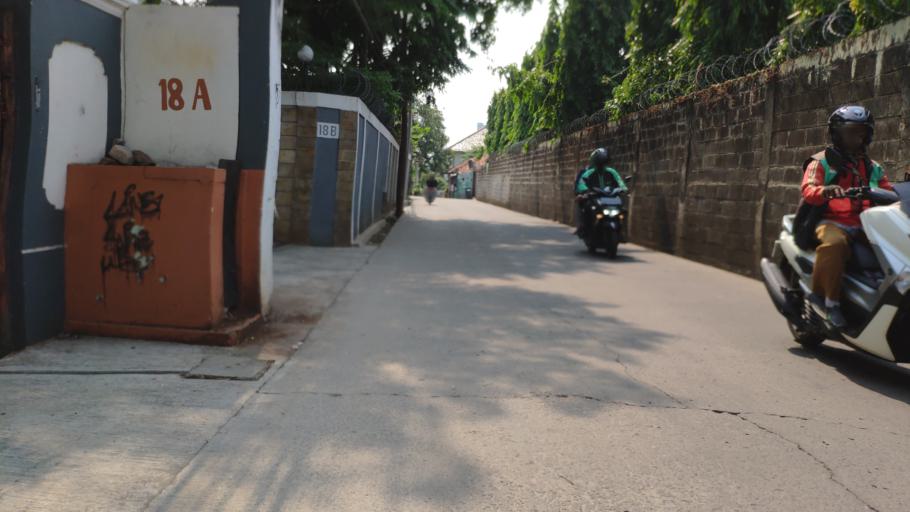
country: ID
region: Jakarta Raya
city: Jakarta
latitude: -6.2658
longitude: 106.8225
